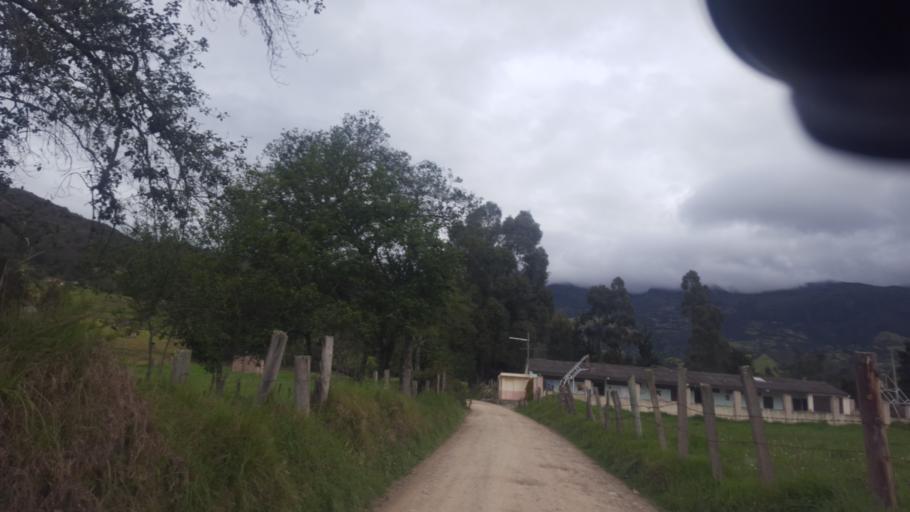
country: CO
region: Boyaca
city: Cerinza
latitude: 5.9732
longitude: -72.9389
